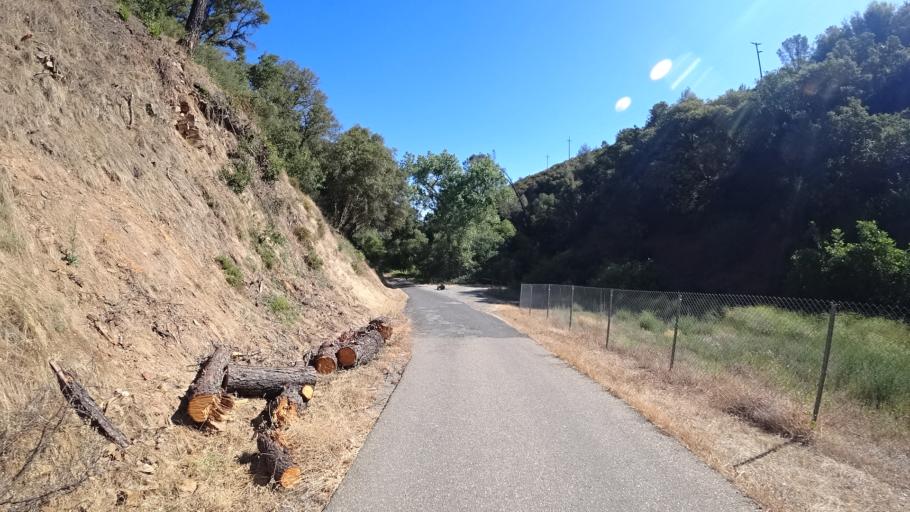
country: US
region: California
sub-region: Amador County
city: Jackson
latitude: 38.2746
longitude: -120.7586
